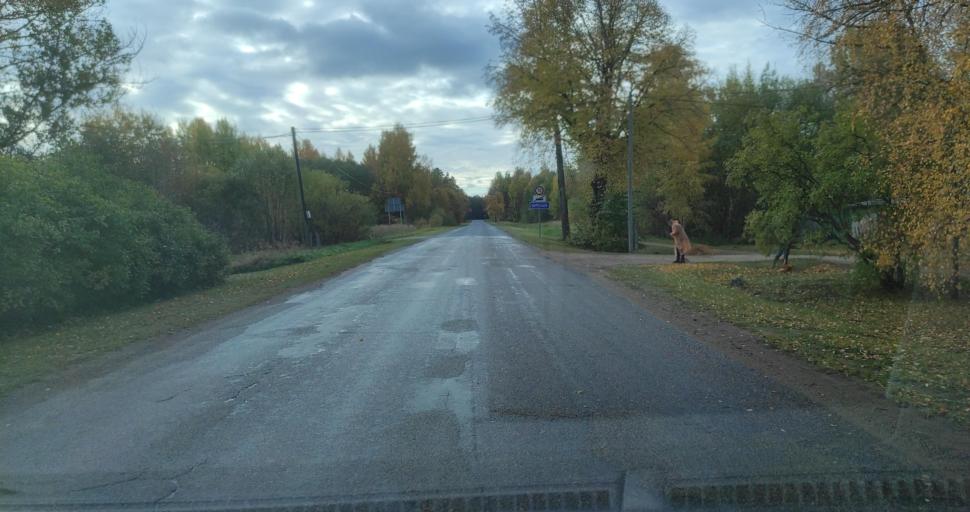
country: LV
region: Skrunda
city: Skrunda
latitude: 56.6668
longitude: 22.0231
